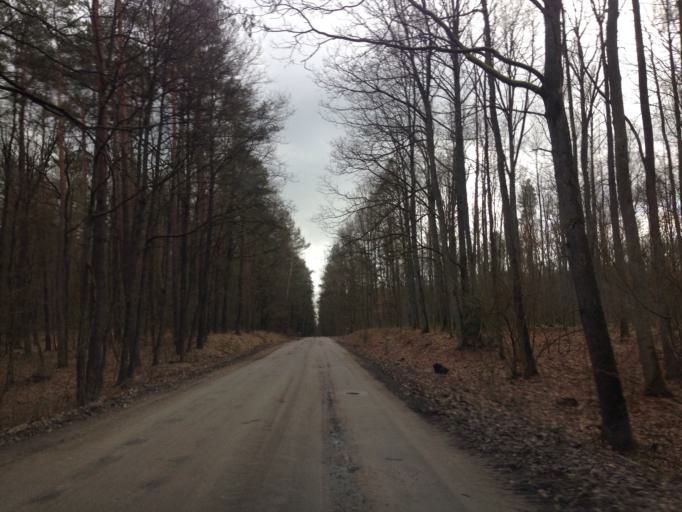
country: PL
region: Kujawsko-Pomorskie
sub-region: Powiat brodnicki
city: Gorzno
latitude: 53.1989
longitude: 19.6938
